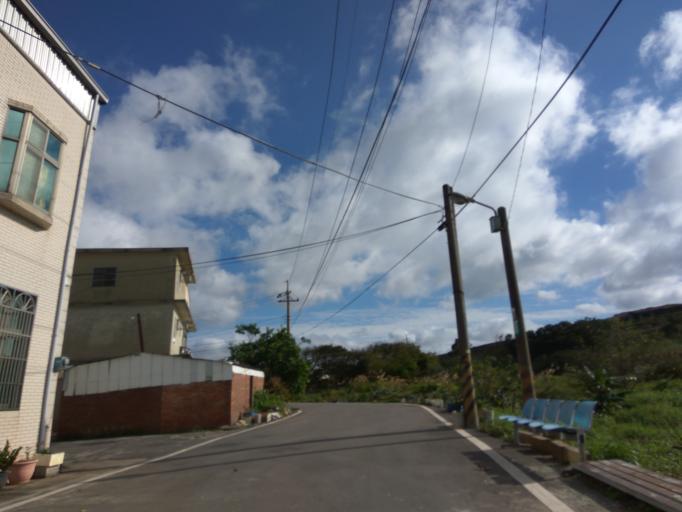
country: TW
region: Taiwan
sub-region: Hsinchu
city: Zhubei
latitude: 24.9723
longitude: 121.0716
